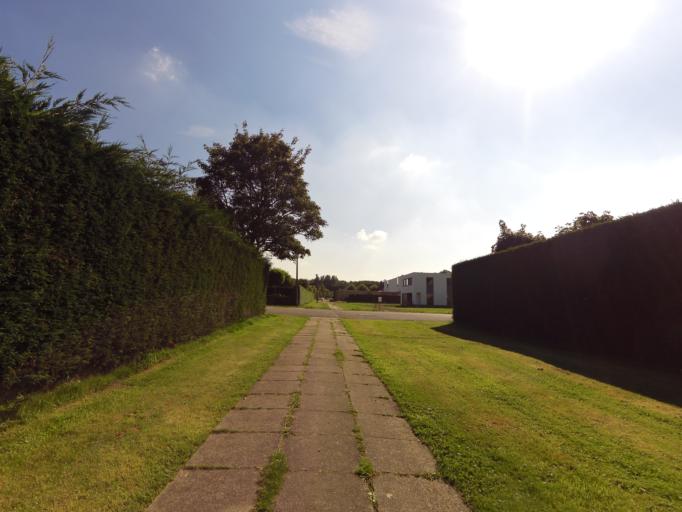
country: BE
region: Flanders
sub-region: Provincie West-Vlaanderen
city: Zuienkerke
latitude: 51.2046
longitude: 3.1579
